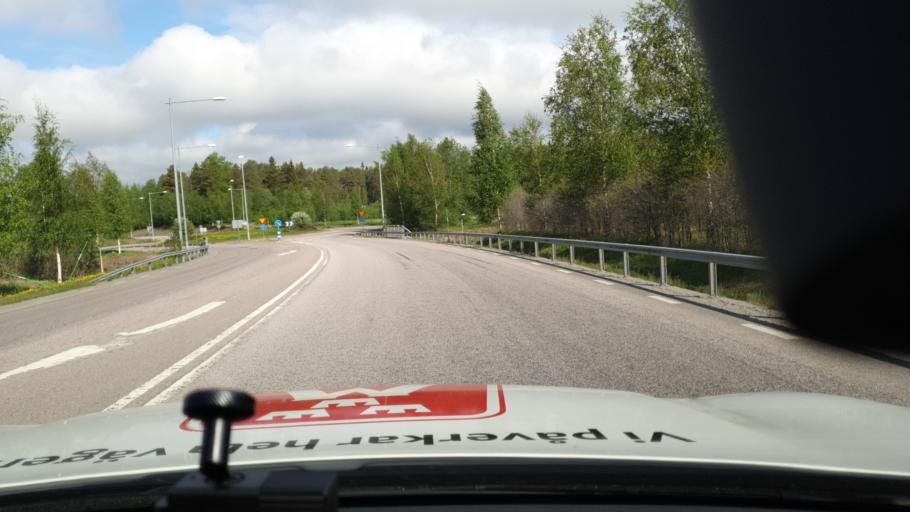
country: SE
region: Vaesterbotten
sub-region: Umea Kommun
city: Umea
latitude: 63.8380
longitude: 20.2509
